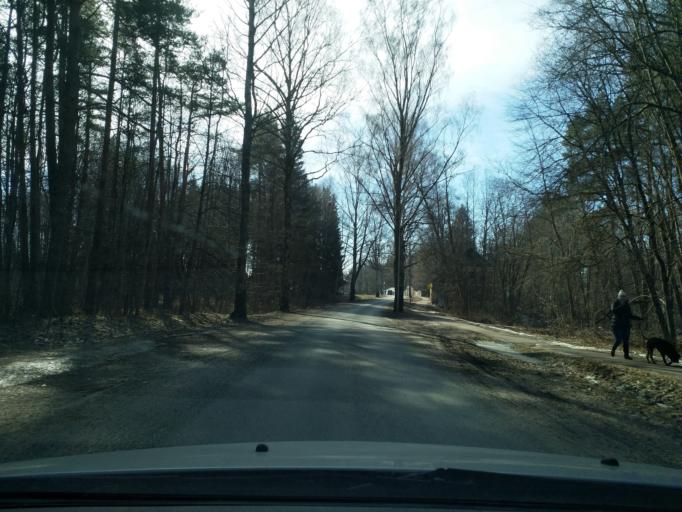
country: LV
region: Valmieras Rajons
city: Valmiera
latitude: 57.5241
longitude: 25.4210
